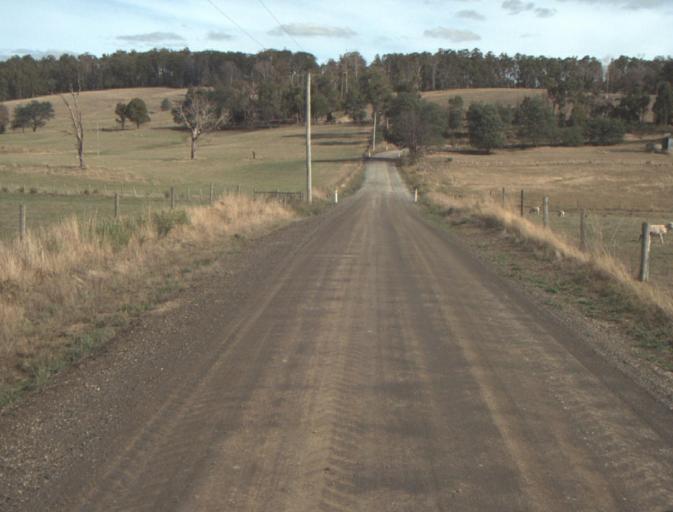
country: AU
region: Tasmania
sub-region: Launceston
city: Mayfield
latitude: -41.2184
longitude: 147.1587
